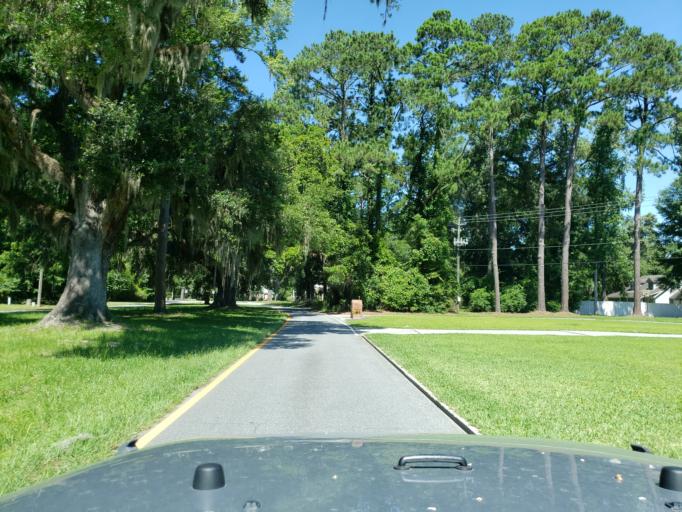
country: US
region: Georgia
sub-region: Chatham County
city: Georgetown
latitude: 31.9716
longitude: -81.2261
